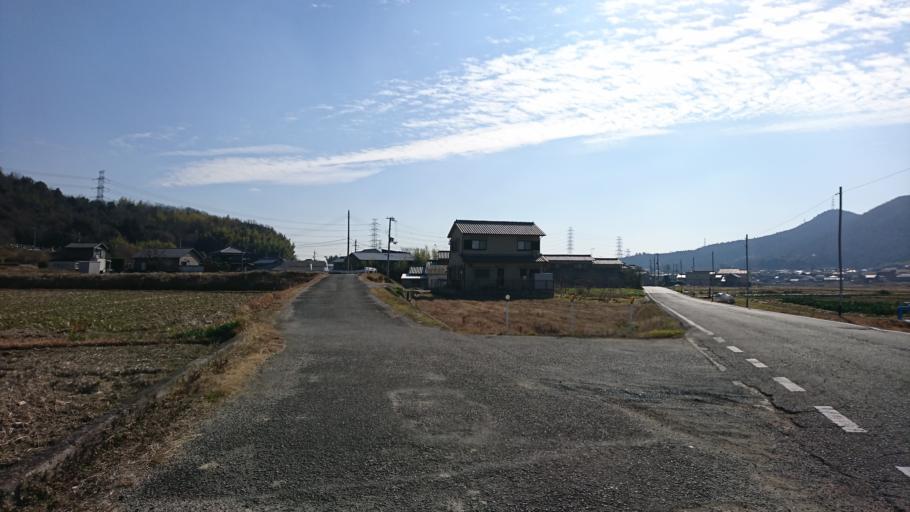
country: JP
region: Hyogo
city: Kakogawacho-honmachi
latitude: 34.8181
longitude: 134.8543
